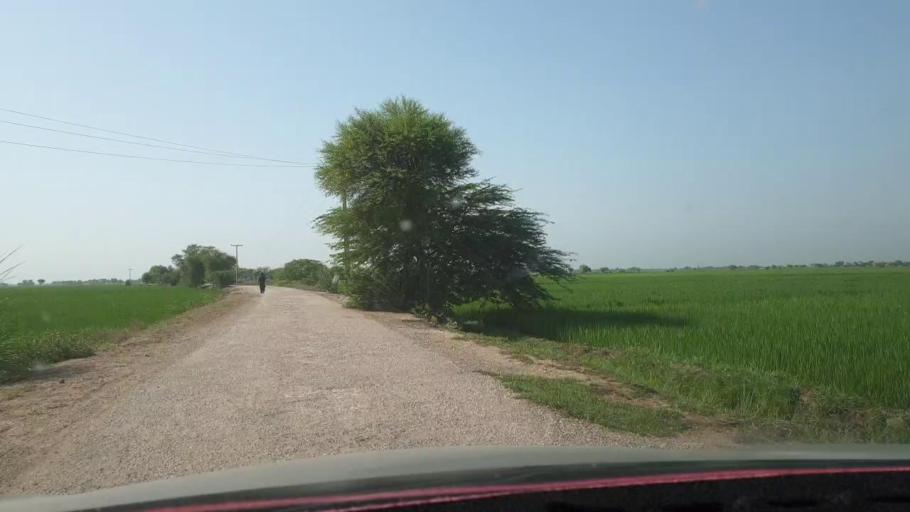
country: PK
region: Sindh
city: Nasirabad
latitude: 27.3772
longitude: 67.8867
